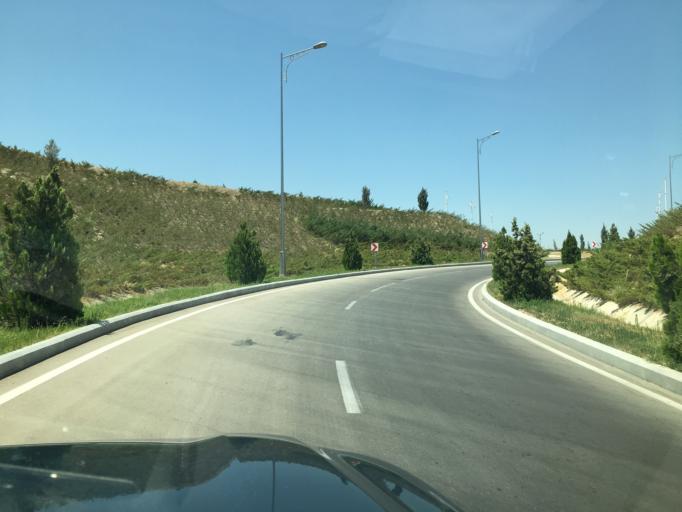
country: TM
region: Ahal
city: Ashgabat
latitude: 37.8709
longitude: 58.3881
